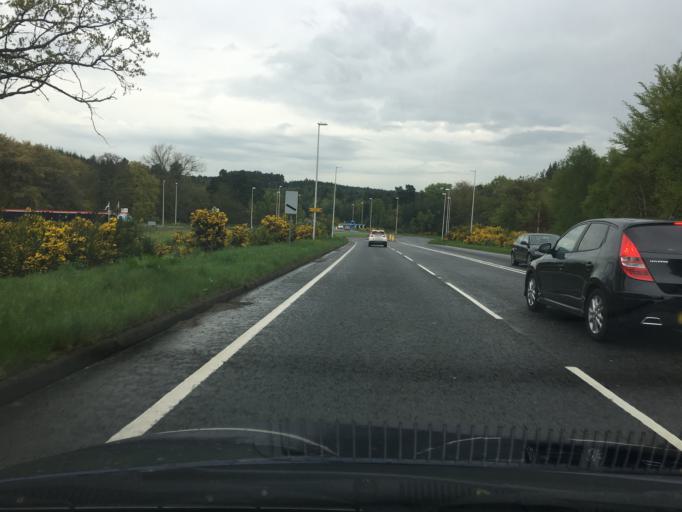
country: GB
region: England
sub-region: Bracknell Forest
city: Crowthorne
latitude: 51.3665
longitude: -0.7665
